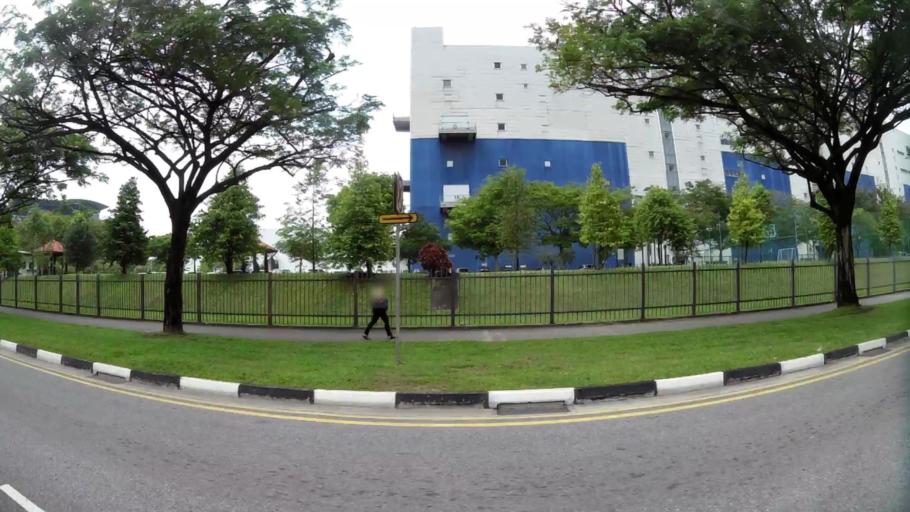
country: SG
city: Singapore
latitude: 1.3598
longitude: 103.9308
